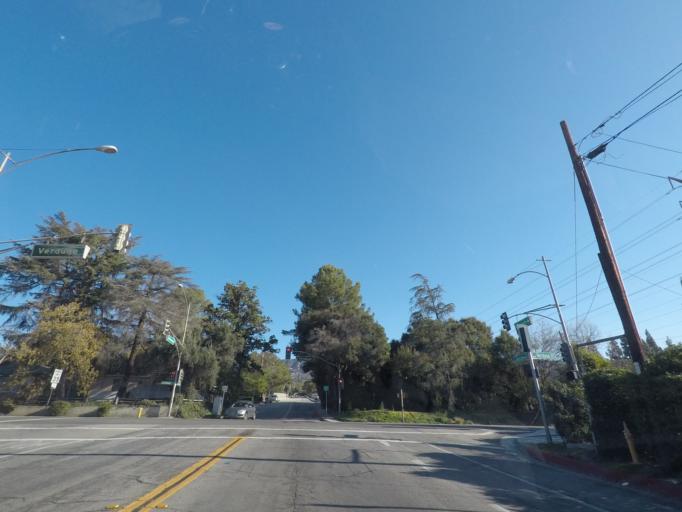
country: US
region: California
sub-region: Los Angeles County
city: La Canada Flintridge
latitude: 34.2054
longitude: -118.2116
